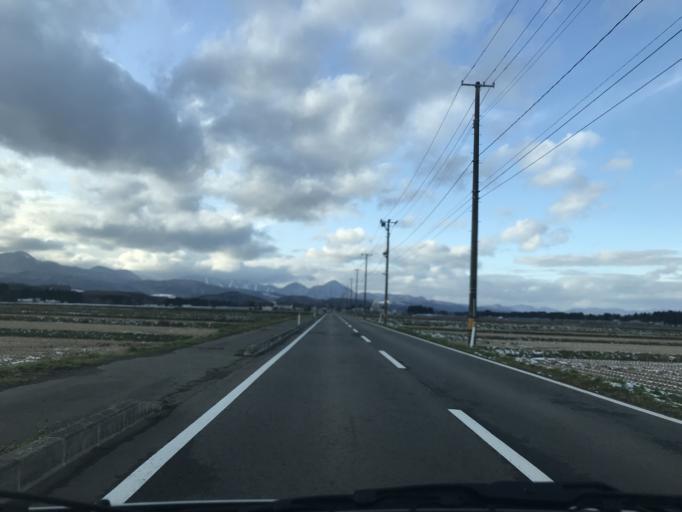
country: JP
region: Iwate
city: Mizusawa
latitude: 39.2002
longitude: 141.0610
